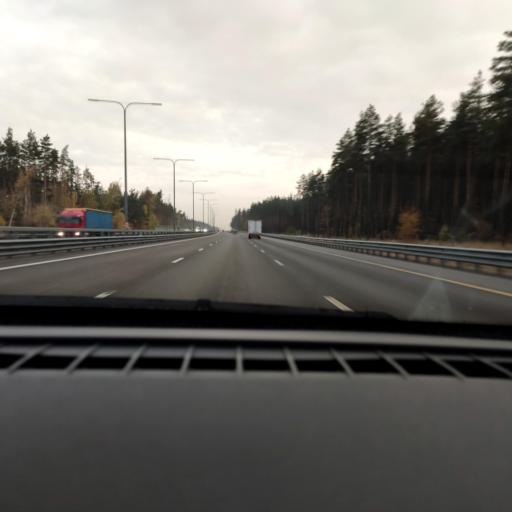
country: RU
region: Voronezj
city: Somovo
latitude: 51.7155
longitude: 39.3081
